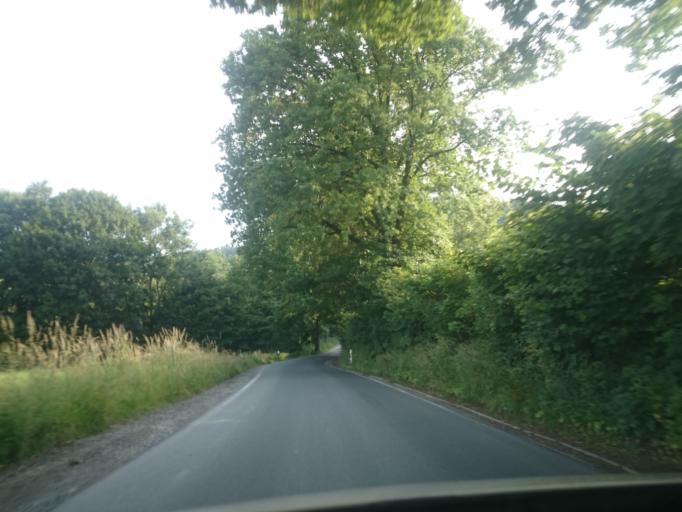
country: DE
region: Saxony
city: Borstendorf
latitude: 50.7760
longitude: 13.1777
